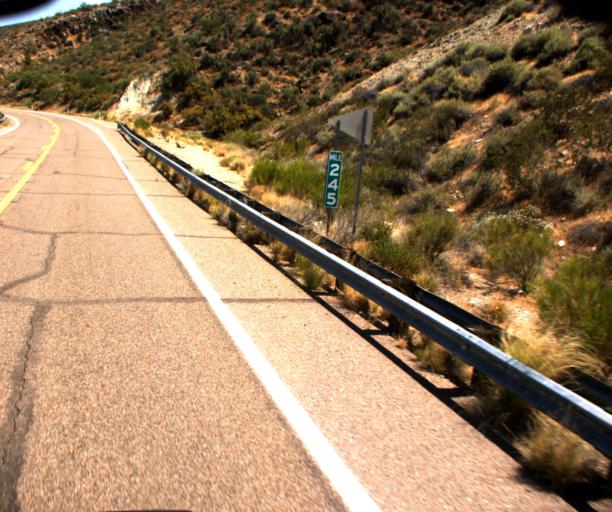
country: US
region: Arizona
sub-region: Gila County
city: Tonto Basin
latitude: 33.6795
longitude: -111.1645
